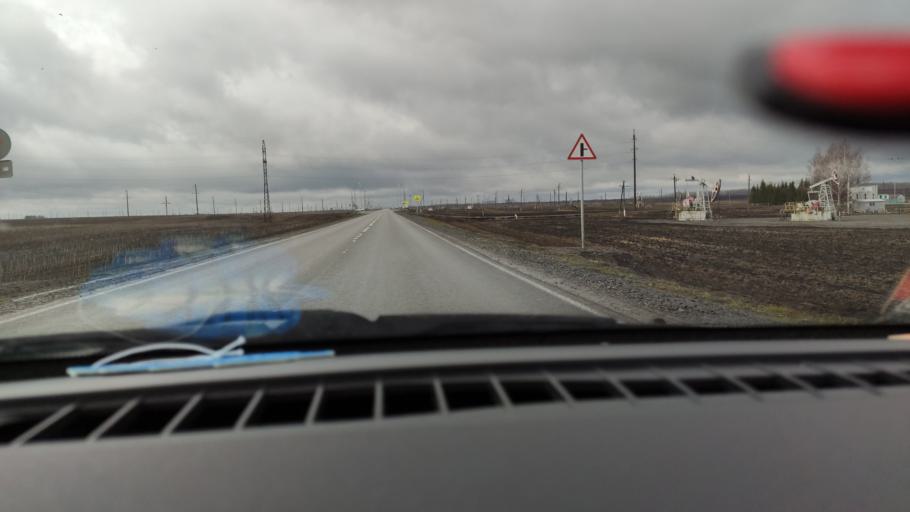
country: RU
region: Tatarstan
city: Nurlat
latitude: 54.4771
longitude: 50.8426
